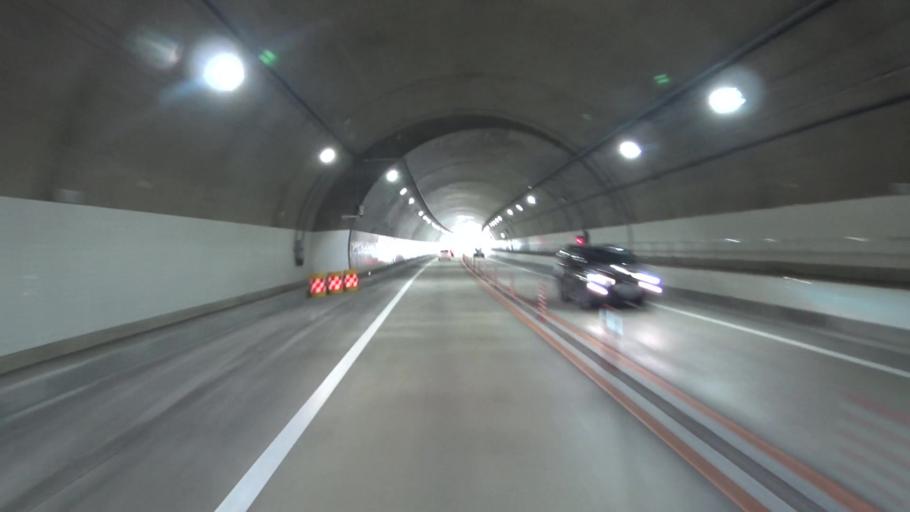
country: JP
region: Kyoto
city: Ayabe
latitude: 35.2520
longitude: 135.3425
